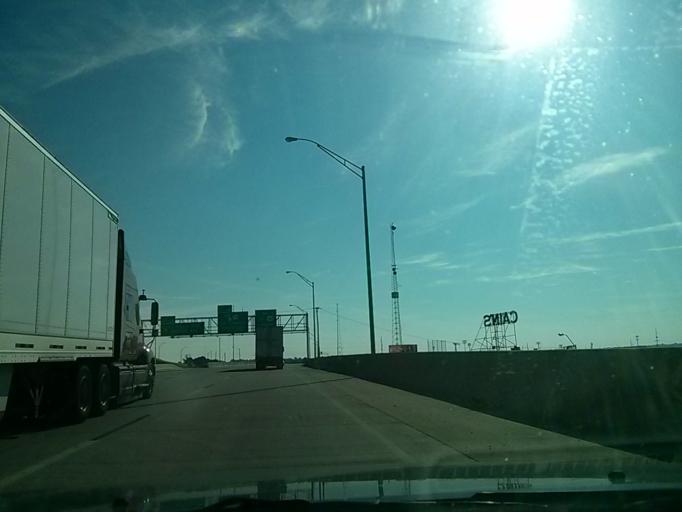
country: US
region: Oklahoma
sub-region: Tulsa County
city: Tulsa
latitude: 36.1611
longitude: -95.9961
